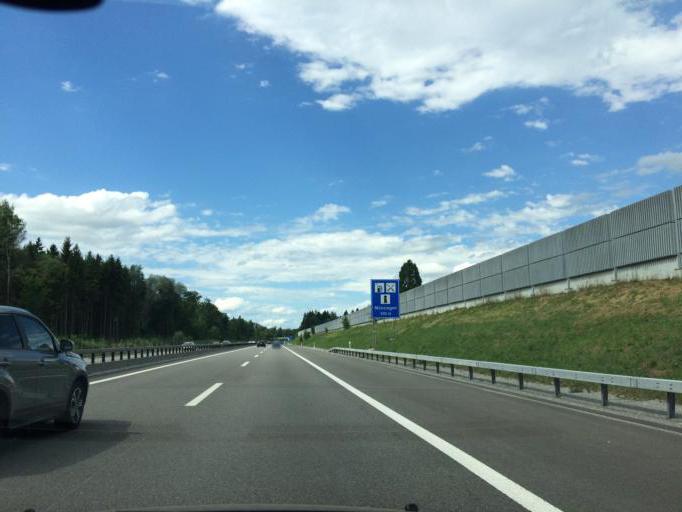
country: CH
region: Bern
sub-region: Bern-Mittelland District
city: Munsingen
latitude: 46.8693
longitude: 7.5473
